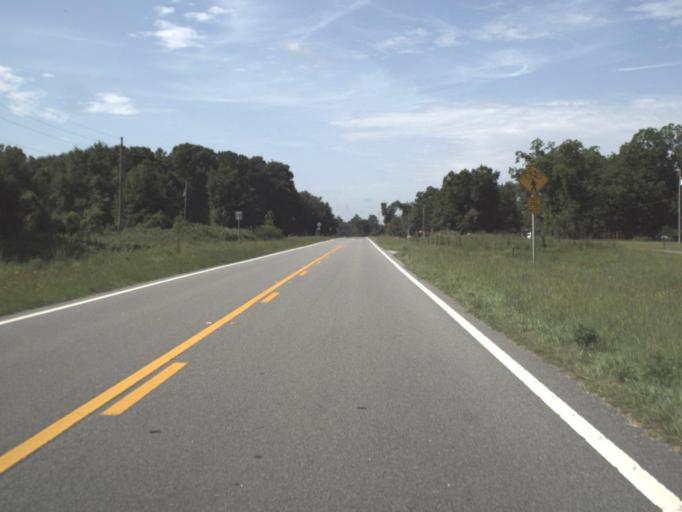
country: US
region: Florida
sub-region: Madison County
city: Madison
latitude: 30.5547
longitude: -83.3672
